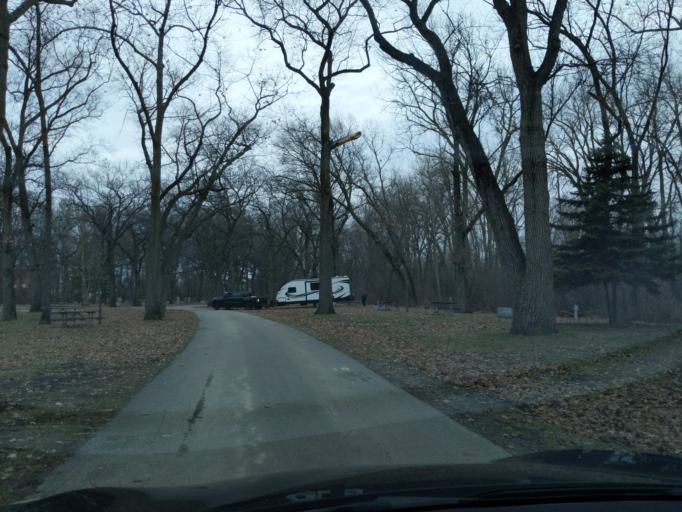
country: US
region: Michigan
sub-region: Bay County
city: Bay City
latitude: 43.6633
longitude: -83.9003
